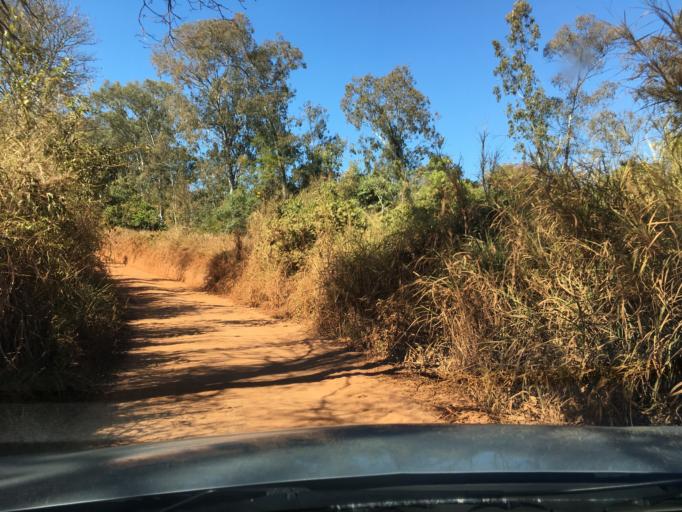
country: BR
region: Minas Gerais
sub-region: Campestre
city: Campestre
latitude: -21.5792
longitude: -46.2044
